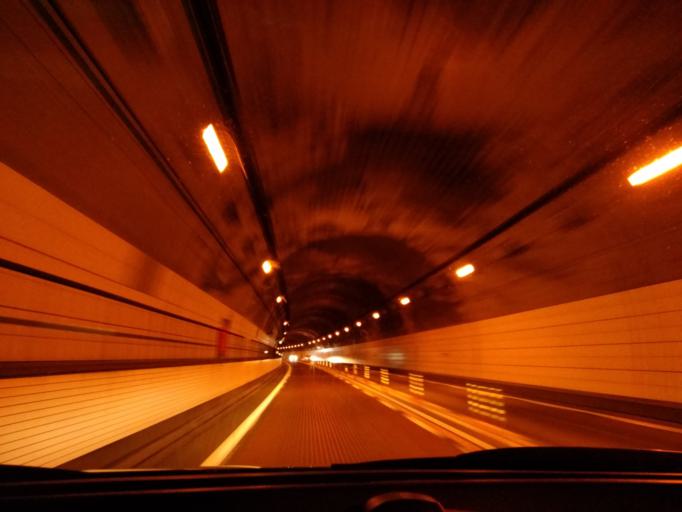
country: JP
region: Akita
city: Yokotemachi
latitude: 39.3058
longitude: 140.7810
